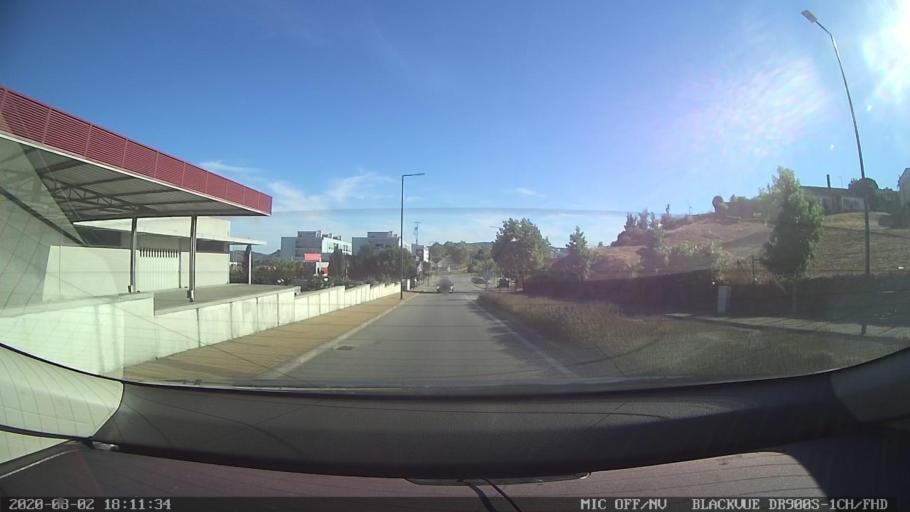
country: PT
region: Vila Real
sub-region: Murca
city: Murca
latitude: 41.4070
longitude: -7.4502
